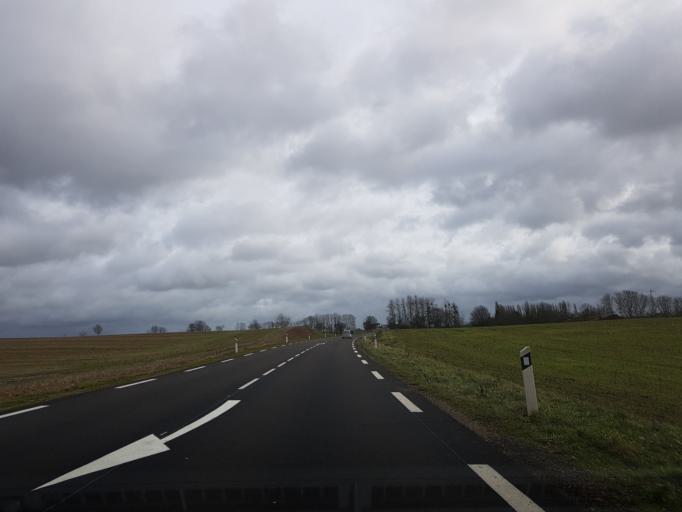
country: FR
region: Champagne-Ardenne
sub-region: Departement de la Haute-Marne
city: Chalindrey
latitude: 47.8531
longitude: 5.4042
